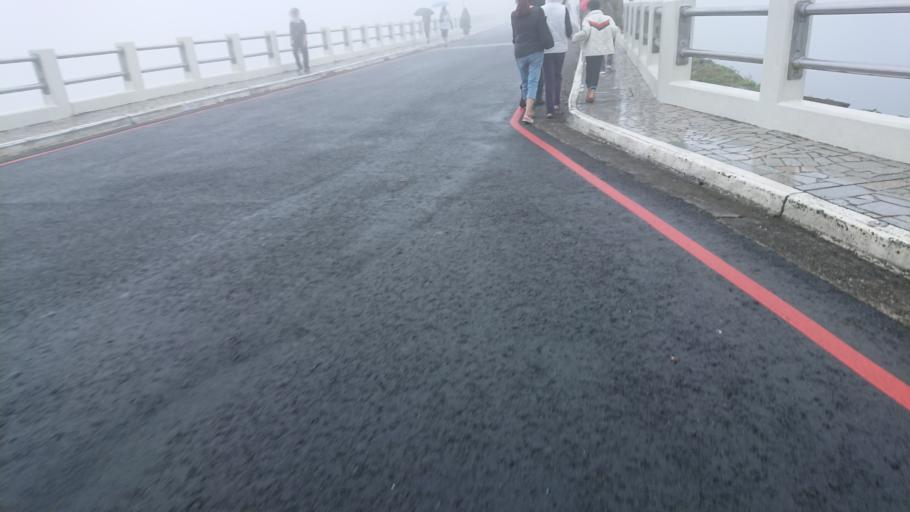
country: TW
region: Taiwan
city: Daxi
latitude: 24.8110
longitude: 121.2408
